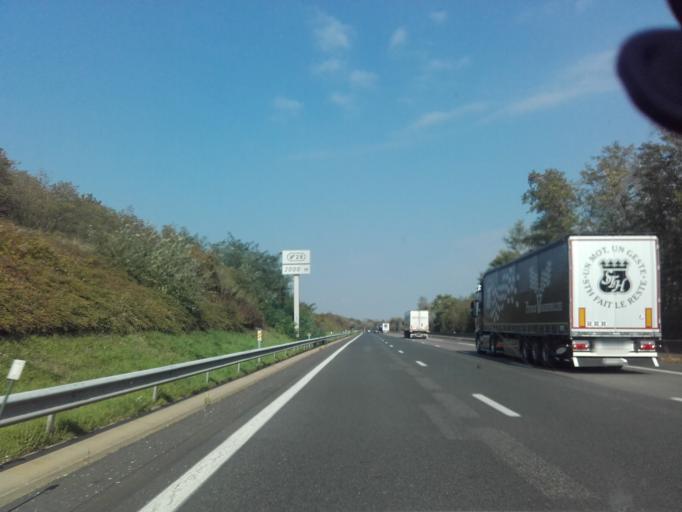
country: FR
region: Bourgogne
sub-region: Departement de Saone-et-Loire
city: Sance
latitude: 46.3467
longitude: 4.8248
